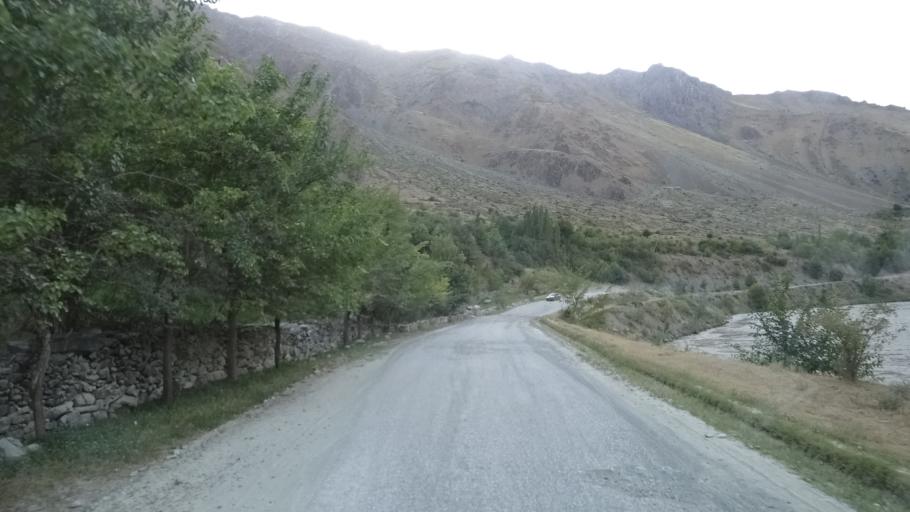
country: TJ
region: Gorno-Badakhshan
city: Qalaikhumb
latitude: 38.3873
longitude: 70.6743
